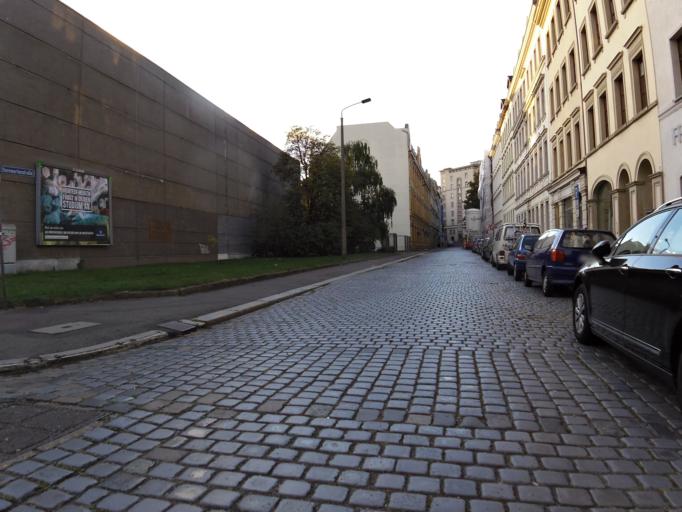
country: DE
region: Saxony
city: Leipzig
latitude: 51.3346
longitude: 12.3816
